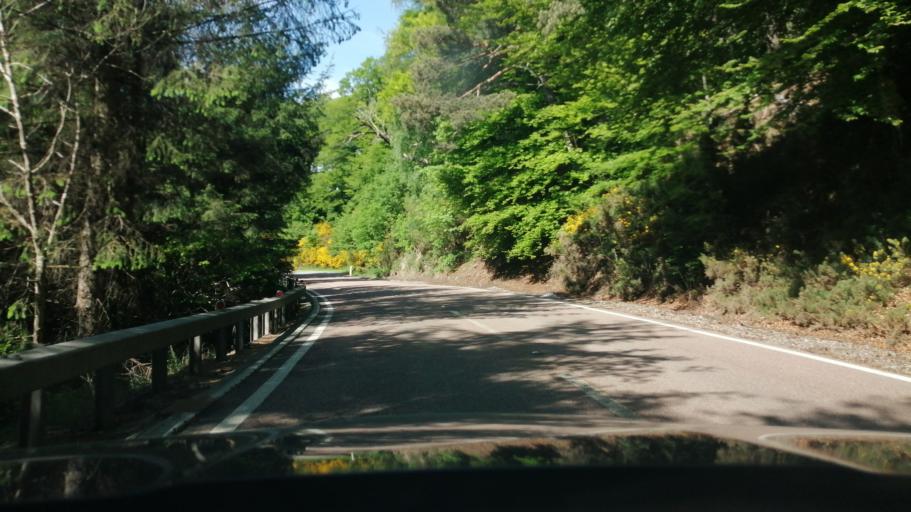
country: GB
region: Scotland
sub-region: Moray
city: Rothes
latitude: 57.4891
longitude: -3.1733
